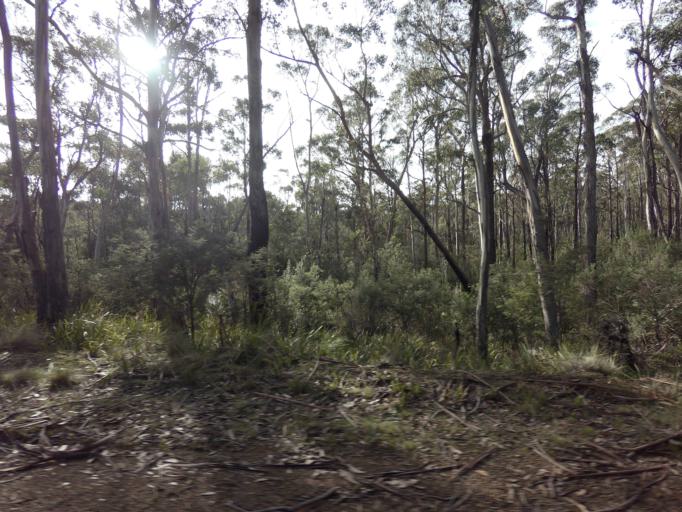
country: AU
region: Tasmania
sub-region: Derwent Valley
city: New Norfolk
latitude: -42.7612
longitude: 146.8938
